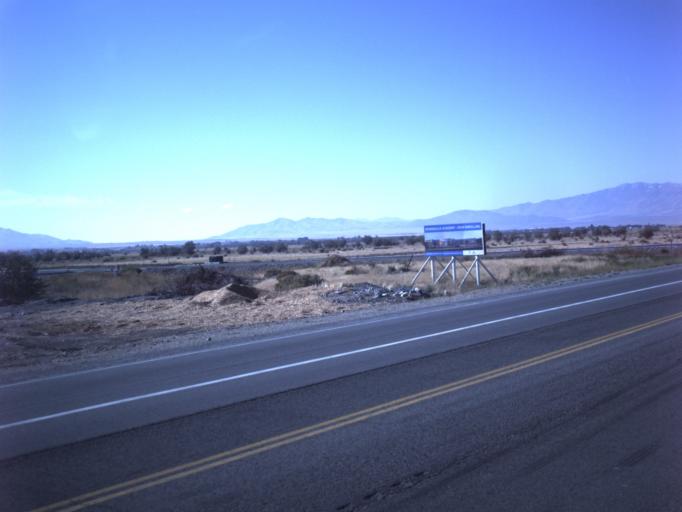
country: US
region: Utah
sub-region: Tooele County
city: Stansbury park
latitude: 40.6378
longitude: -112.3247
